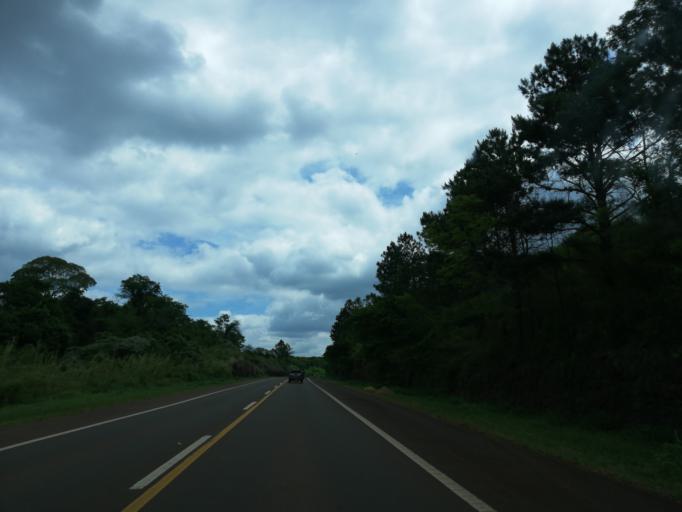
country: AR
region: Misiones
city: Arroyo del Medio
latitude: -27.6436
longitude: -55.4001
